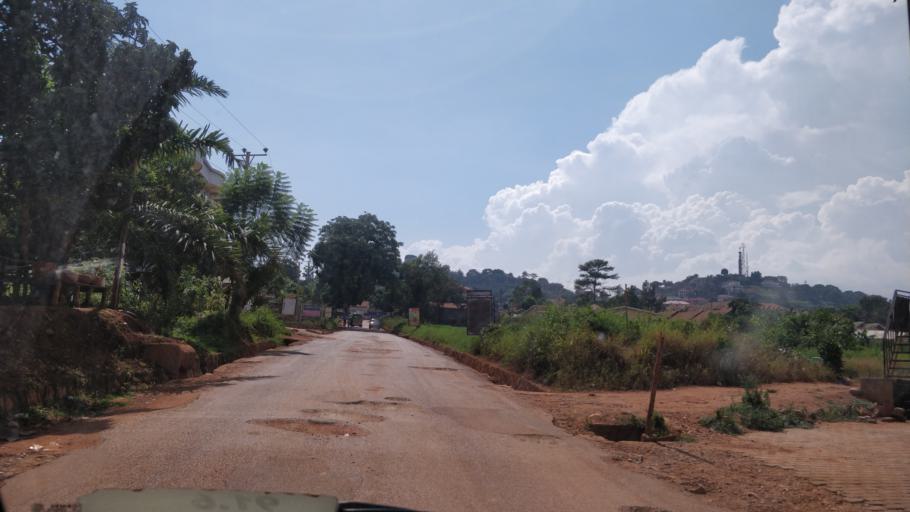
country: UG
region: Central Region
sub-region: Kampala District
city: Kampala
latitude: 0.2686
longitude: 32.6159
